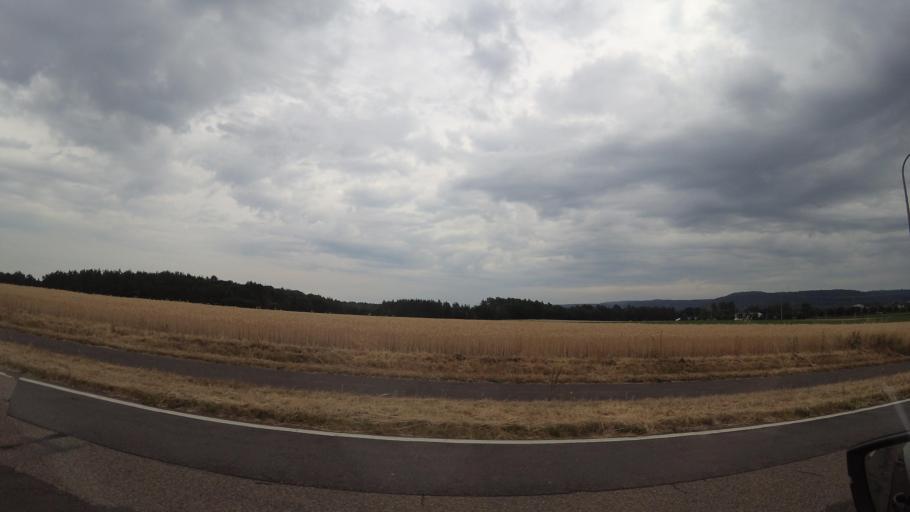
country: DE
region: Rheinland-Pfalz
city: Bruchmuhlbach-Miesau
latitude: 49.4127
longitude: 7.4348
